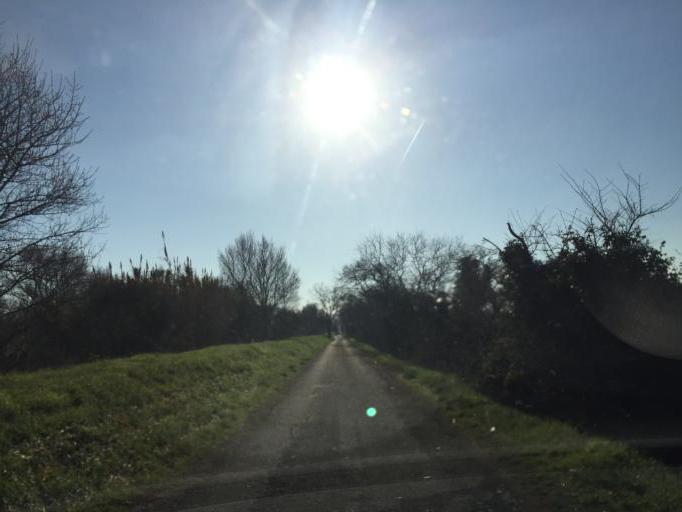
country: FR
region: Provence-Alpes-Cote d'Azur
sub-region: Departement du Vaucluse
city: Sarrians
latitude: 44.0693
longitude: 4.9300
